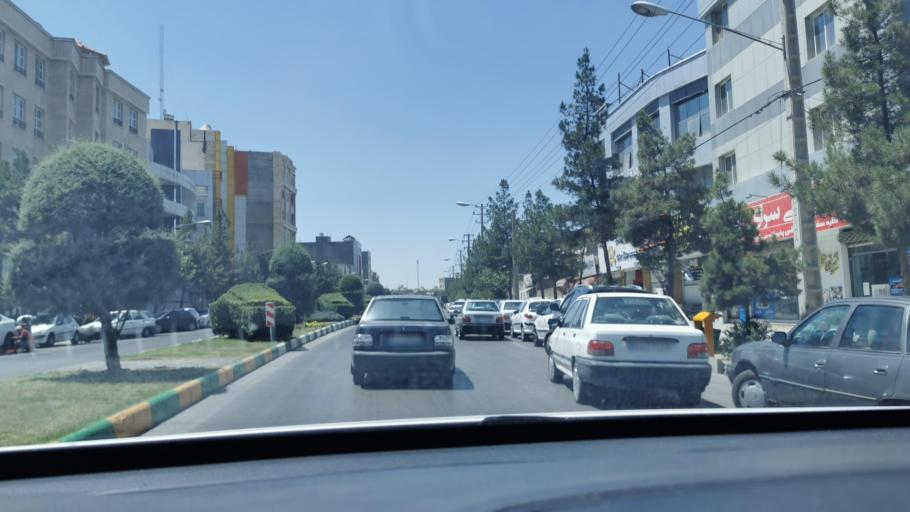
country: IR
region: Razavi Khorasan
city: Mashhad
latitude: 36.3383
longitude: 59.4865
